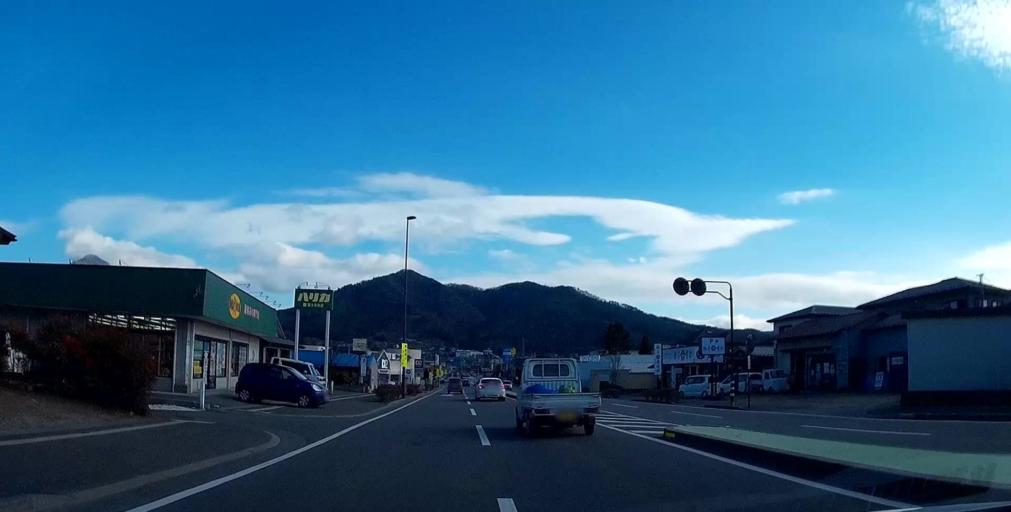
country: JP
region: Yamanashi
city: Fujikawaguchiko
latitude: 35.4831
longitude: 138.8072
